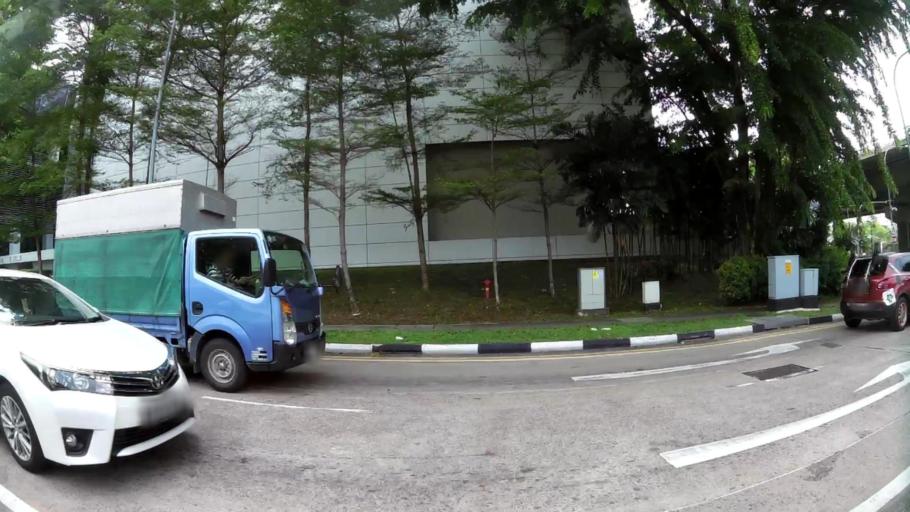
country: SG
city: Singapore
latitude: 1.3527
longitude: 103.9646
